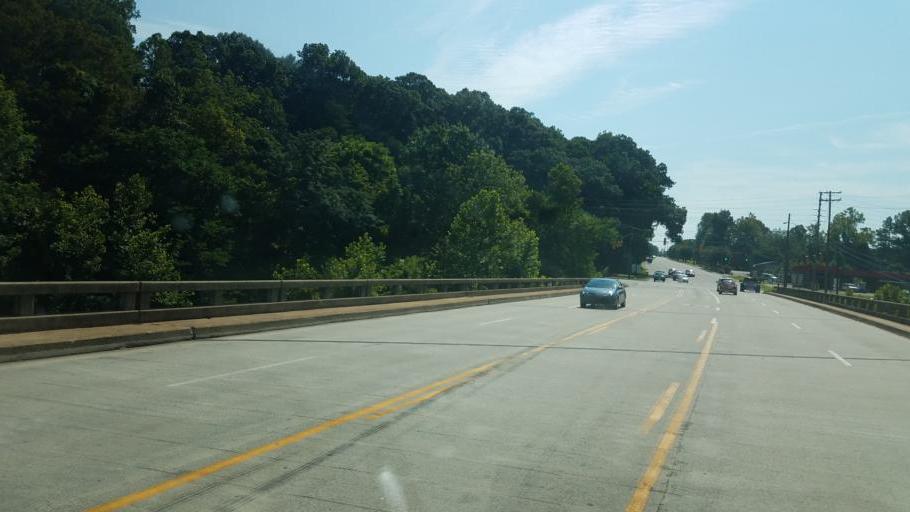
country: US
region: North Carolina
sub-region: Burke County
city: Morganton
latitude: 35.7498
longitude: -81.7058
